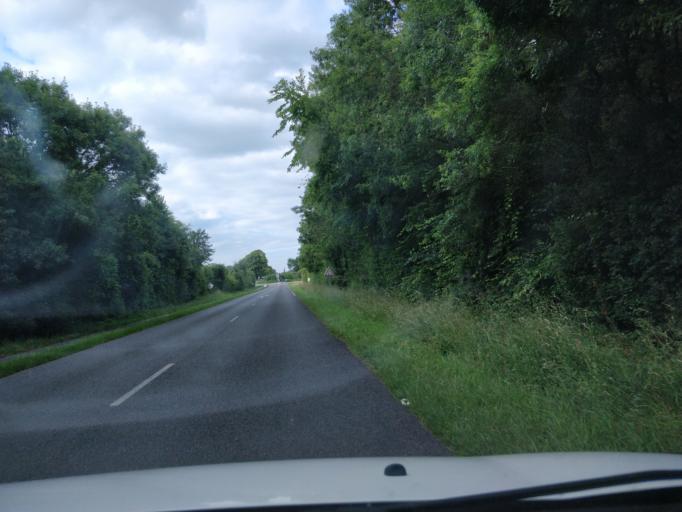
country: FR
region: Pays de la Loire
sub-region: Departement de Maine-et-Loire
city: Feneu
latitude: 47.5633
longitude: -0.5976
